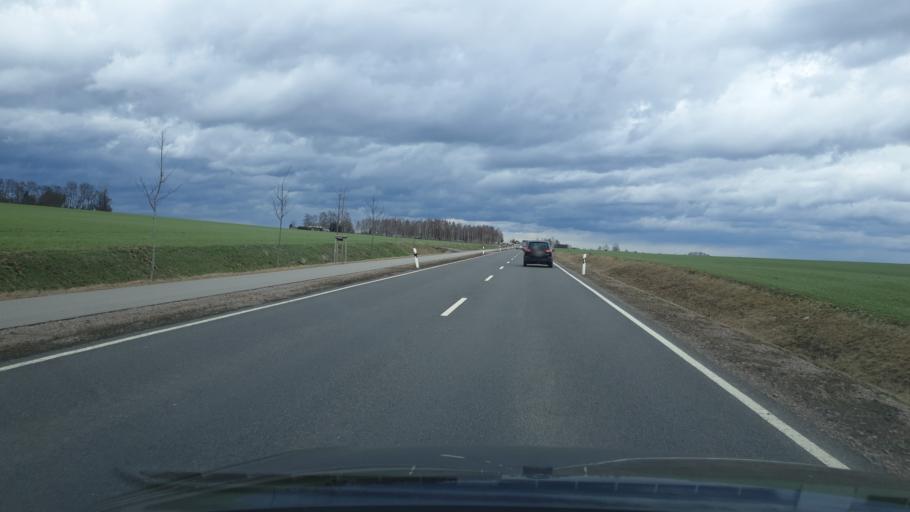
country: DE
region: Saxony
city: Claussnitz
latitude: 50.9505
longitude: 12.9104
